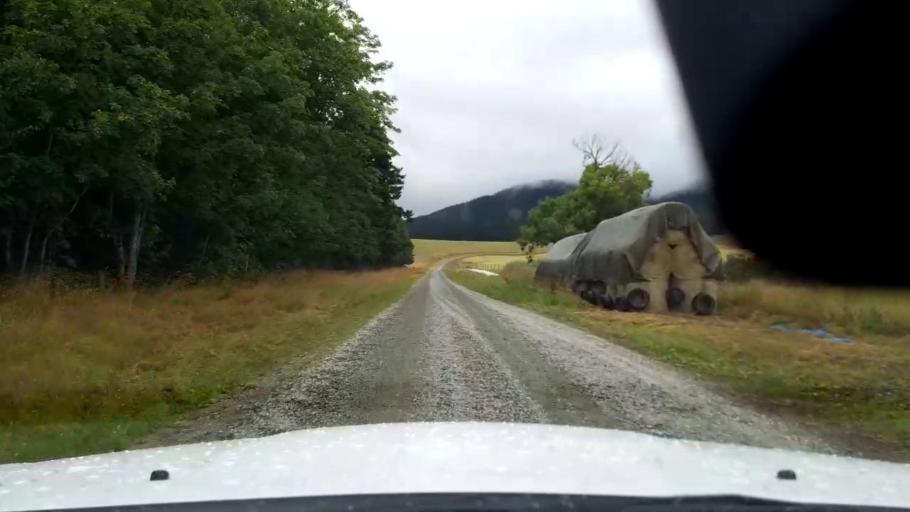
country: NZ
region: Canterbury
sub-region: Timaru District
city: Pleasant Point
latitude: -44.0727
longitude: 171.1496
